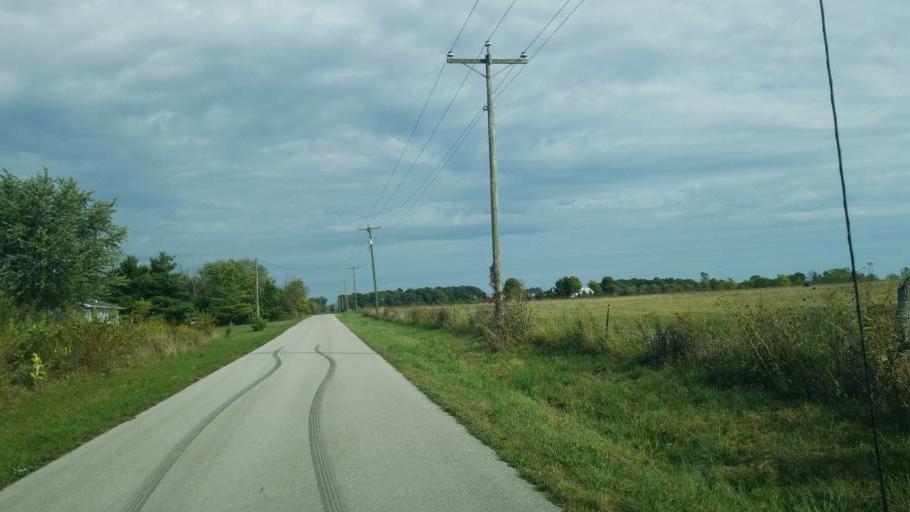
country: US
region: Ohio
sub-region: Hancock County
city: Arlington
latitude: 40.8771
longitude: -83.5871
